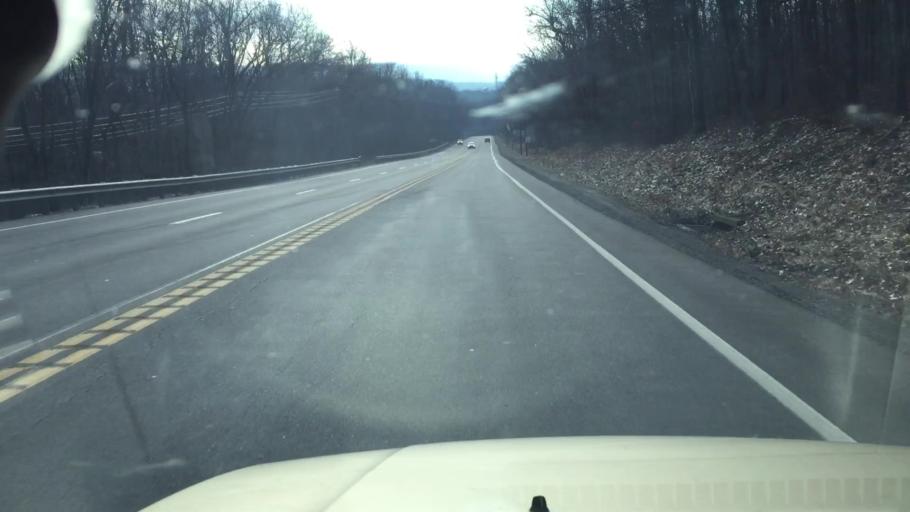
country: US
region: Pennsylvania
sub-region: Luzerne County
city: Freeland
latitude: 41.0713
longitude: -75.9590
